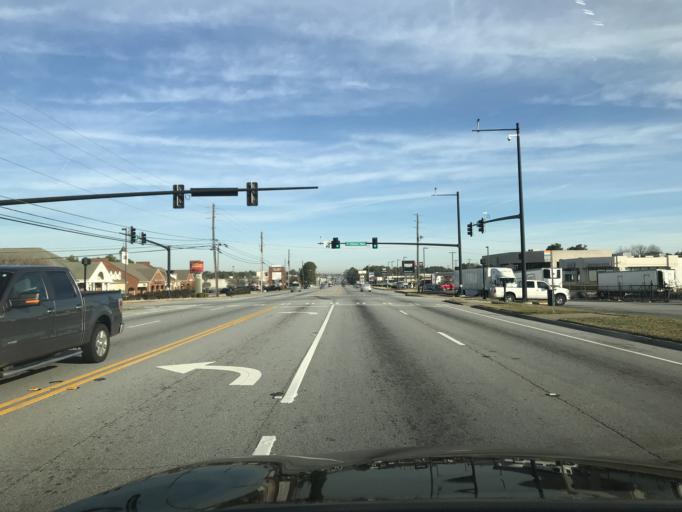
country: US
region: Georgia
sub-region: Clayton County
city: Morrow
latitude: 33.5591
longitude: -84.3457
